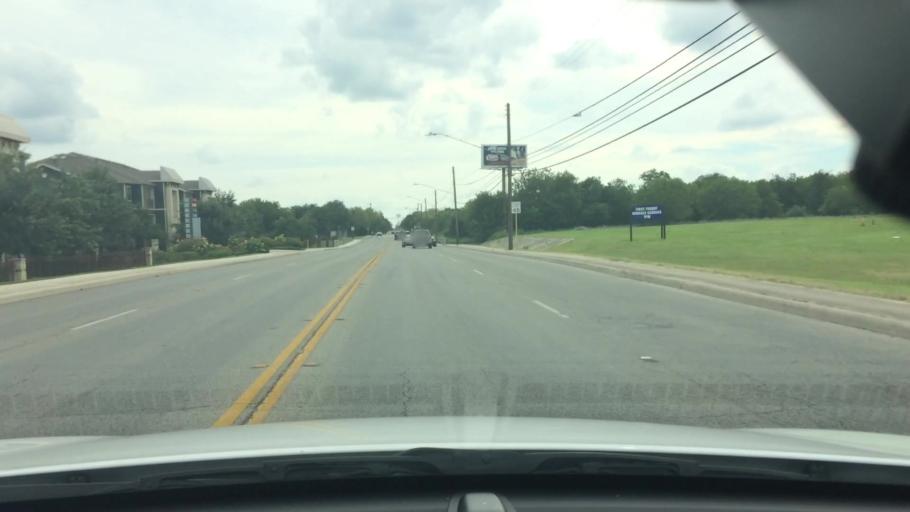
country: US
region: Texas
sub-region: Bexar County
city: Leon Valley
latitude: 29.5126
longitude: -98.6110
